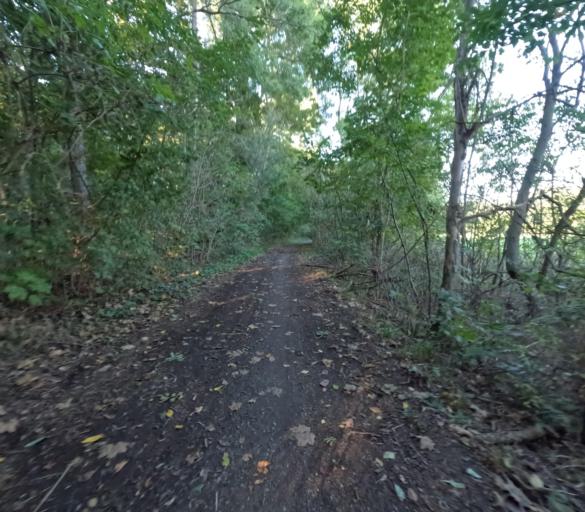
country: DE
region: Saxony
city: Schkeuditz
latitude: 51.3683
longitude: 12.2319
